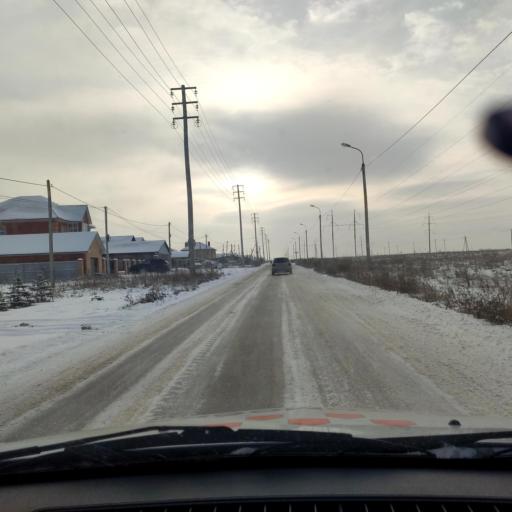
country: RU
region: Bashkortostan
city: Kabakovo
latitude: 54.6153
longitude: 56.0892
